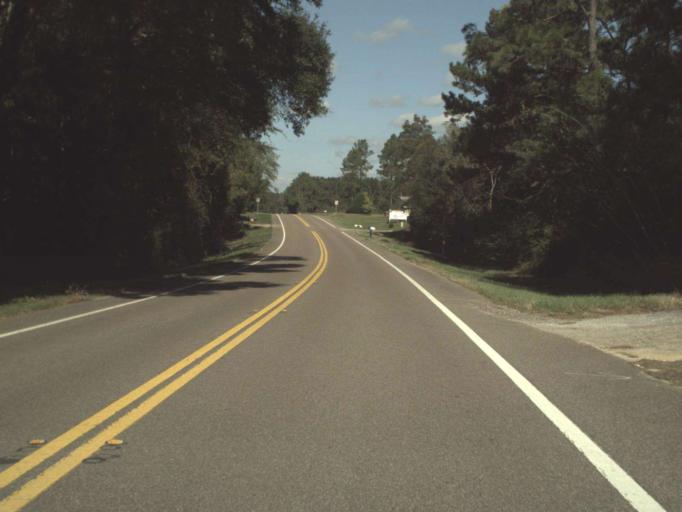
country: US
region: Florida
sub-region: Walton County
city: DeFuniak Springs
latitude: 30.8656
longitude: -86.1164
